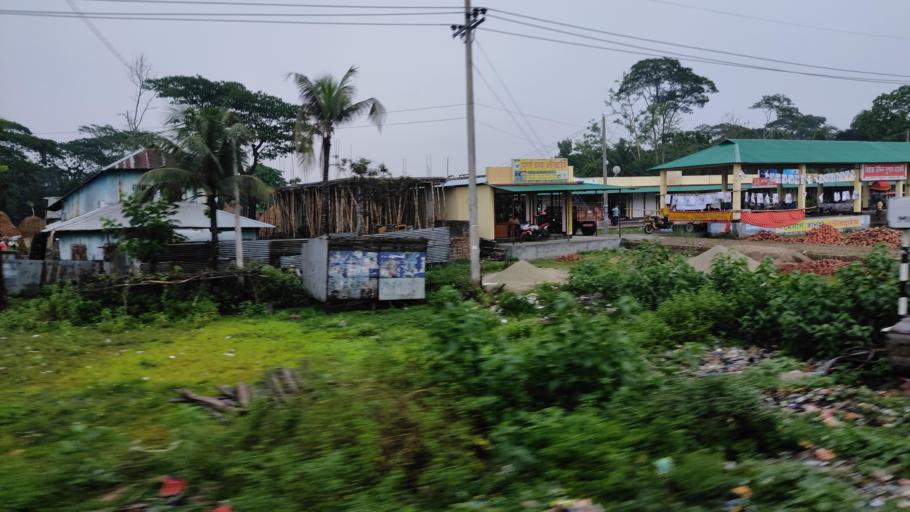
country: BD
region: Barisal
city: Bhandaria
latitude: 22.3162
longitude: 90.3255
